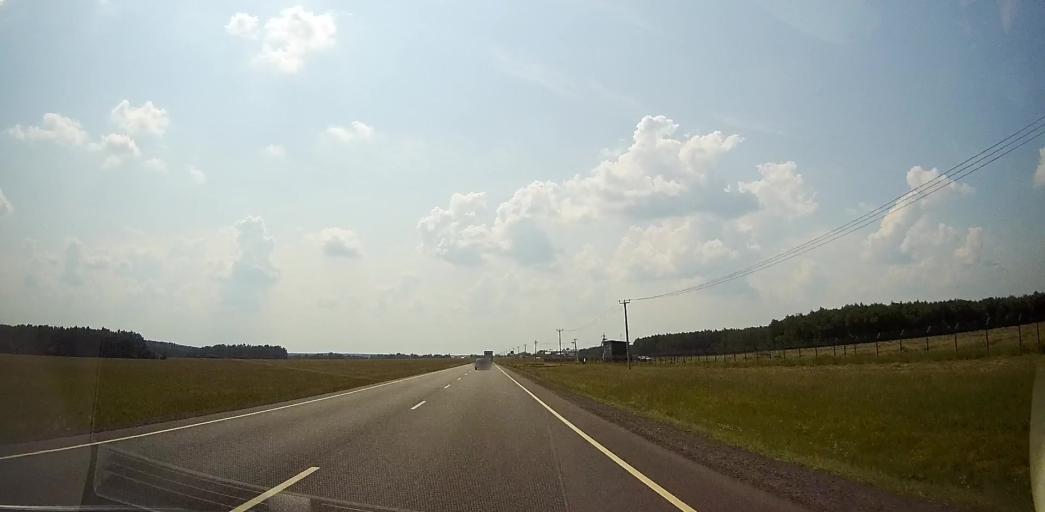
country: RU
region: Moskovskaya
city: Meshcherino
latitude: 55.1563
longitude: 38.3081
